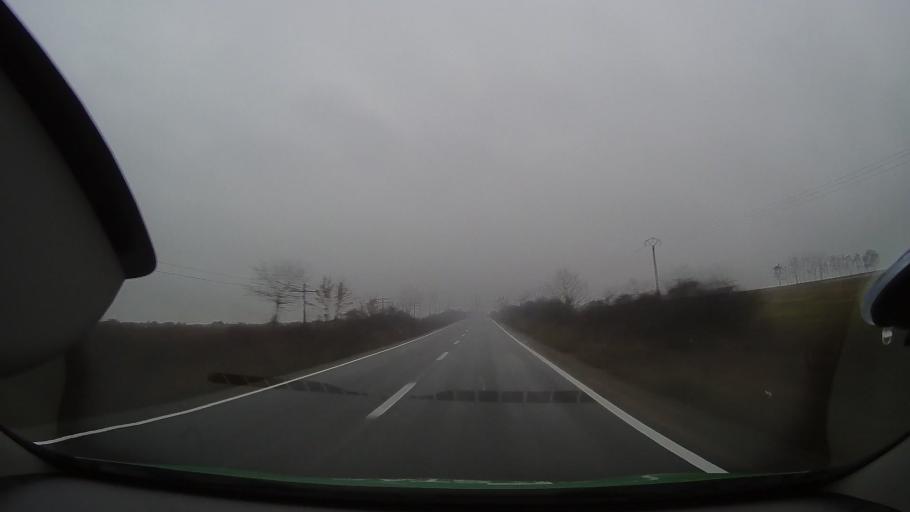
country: RO
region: Bihor
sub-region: Comuna Olcea
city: Calacea
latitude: 46.7196
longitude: 21.9513
